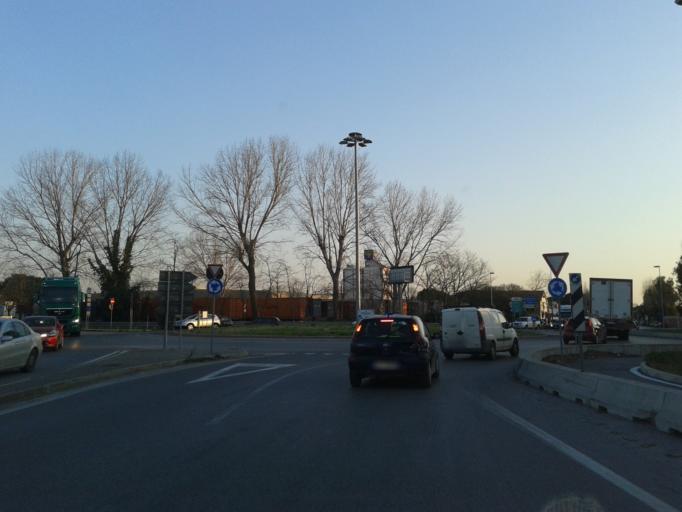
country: IT
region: Tuscany
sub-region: Provincia di Livorno
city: Livorno
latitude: 43.5860
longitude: 10.3457
